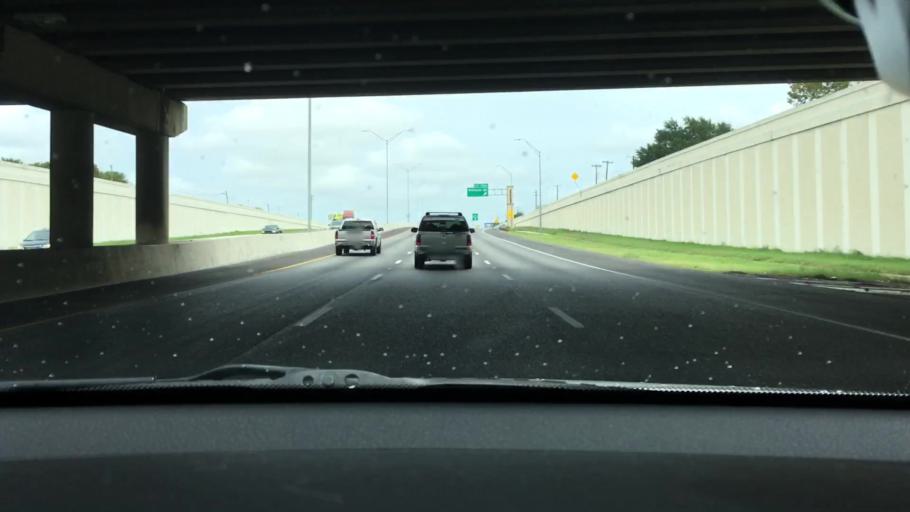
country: US
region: Texas
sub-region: Bexar County
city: Kirby
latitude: 29.4616
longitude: -98.4104
